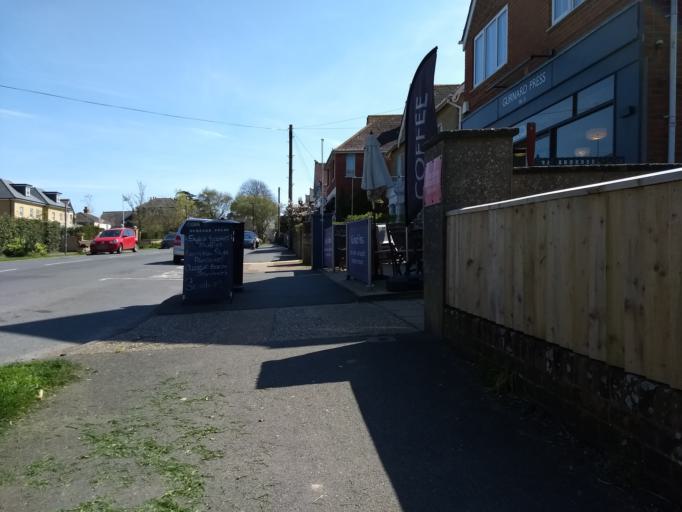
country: GB
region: England
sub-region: Isle of Wight
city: Gurnard
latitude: 50.7564
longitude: -1.3225
